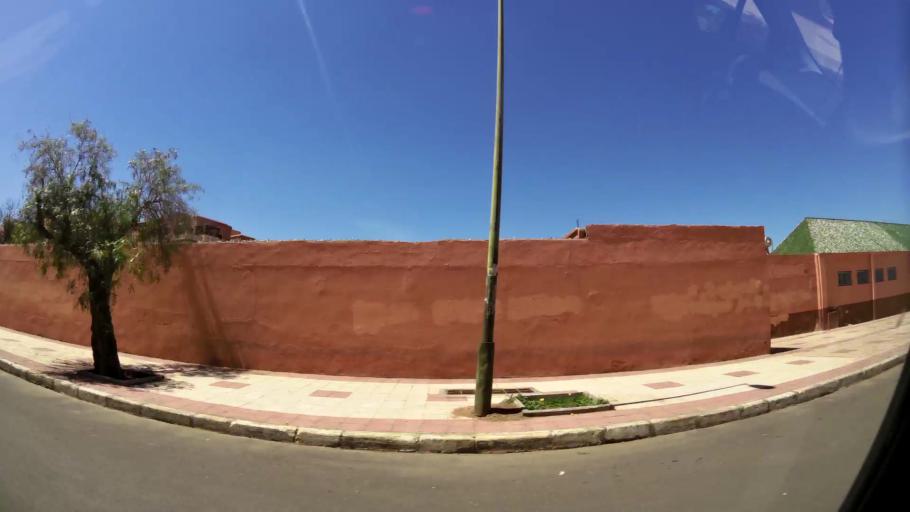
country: MA
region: Marrakech-Tensift-Al Haouz
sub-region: Marrakech
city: Marrakesh
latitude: 31.6267
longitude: -8.0063
